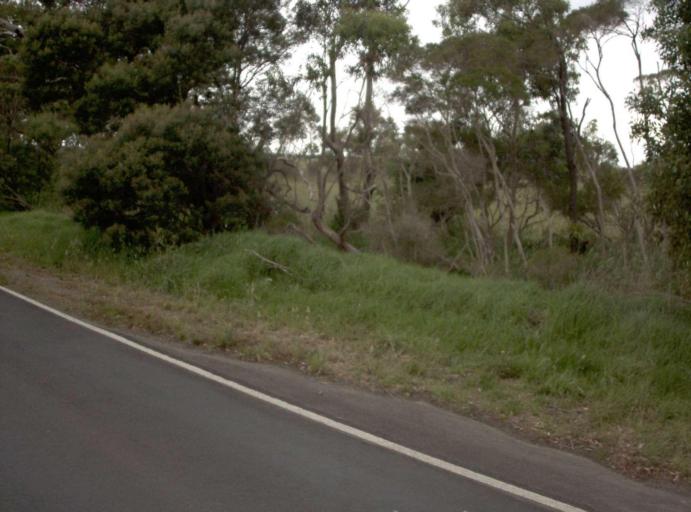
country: AU
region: Victoria
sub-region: Latrobe
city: Traralgon
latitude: -38.5525
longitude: 146.7458
